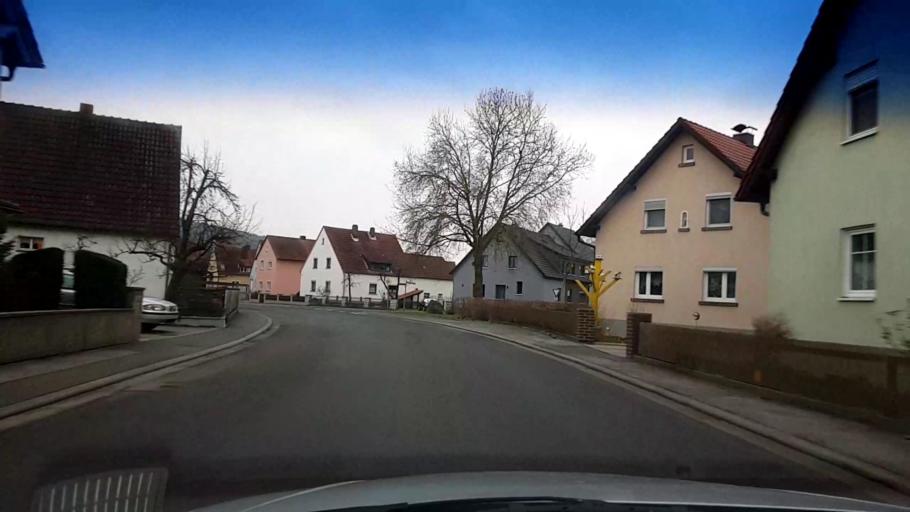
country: DE
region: Bavaria
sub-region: Upper Franconia
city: Rattelsdorf
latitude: 50.0074
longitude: 10.9068
